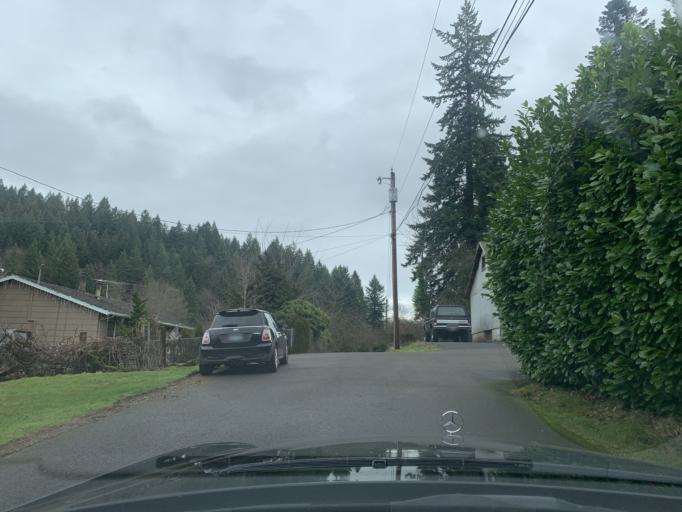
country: US
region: Oregon
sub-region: Clackamas County
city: Happy Valley
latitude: 45.4428
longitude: -122.5139
